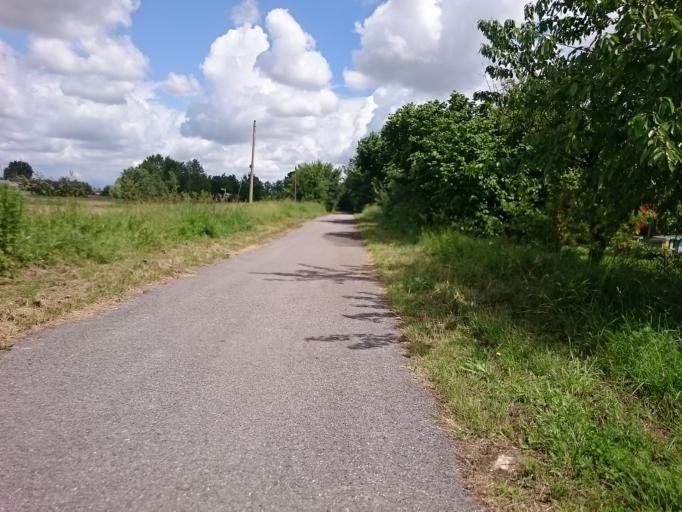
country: IT
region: Veneto
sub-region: Provincia di Padova
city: Campodoro
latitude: 45.5031
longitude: 11.7443
